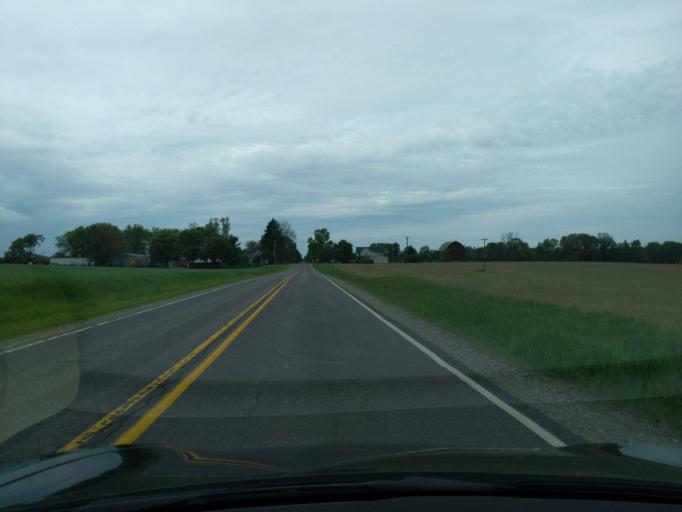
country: US
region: Michigan
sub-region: Ingham County
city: Leslie
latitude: 42.4752
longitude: -84.3561
